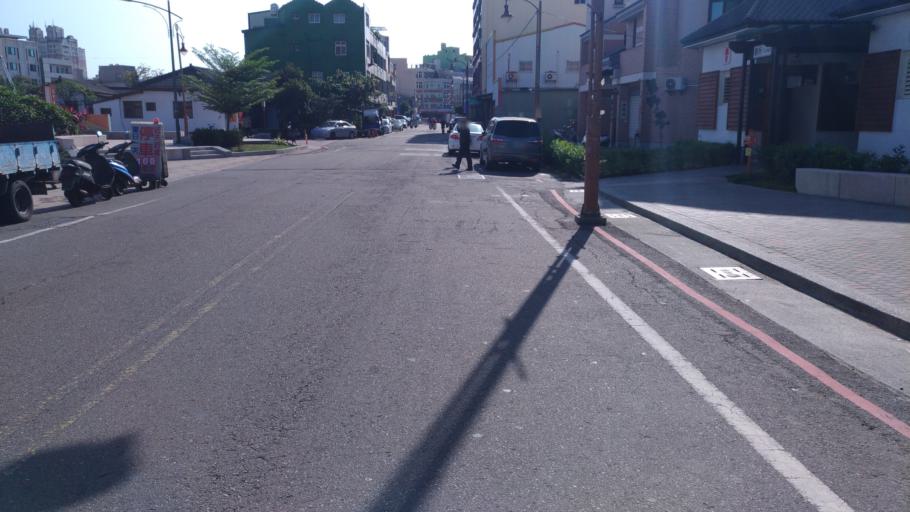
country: TW
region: Taiwan
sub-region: Changhua
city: Chang-hua
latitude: 24.0564
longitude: 120.4303
